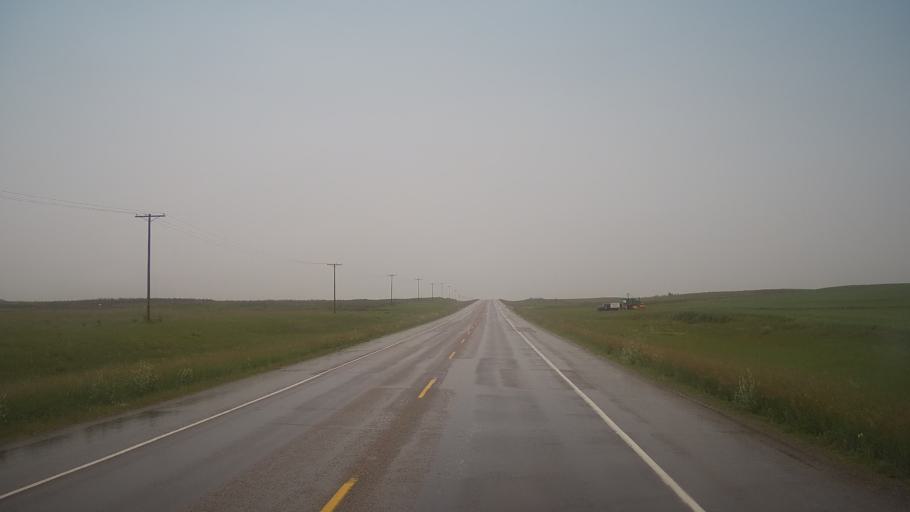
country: CA
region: Saskatchewan
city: Biggar
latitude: 52.0767
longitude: -108.0241
